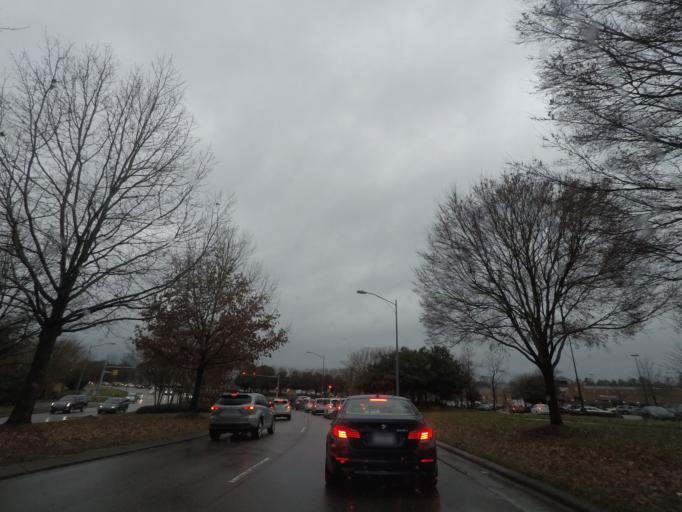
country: US
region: North Carolina
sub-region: Durham County
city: Durham
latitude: 35.9028
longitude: -78.9442
